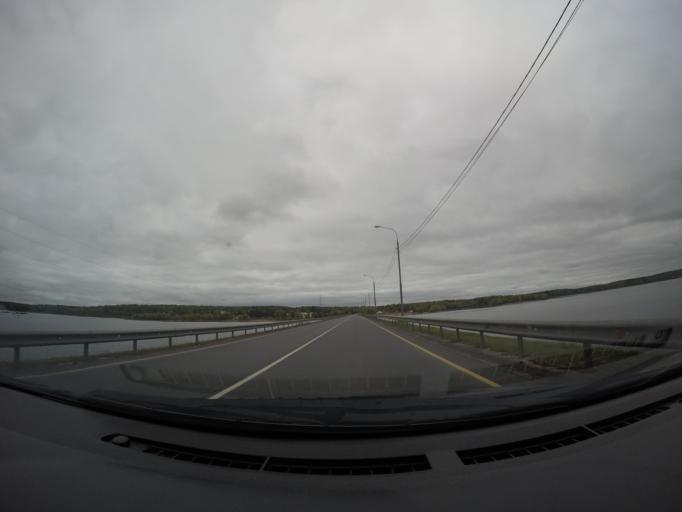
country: RU
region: Moskovskaya
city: Ruza
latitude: 55.7640
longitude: 36.2620
